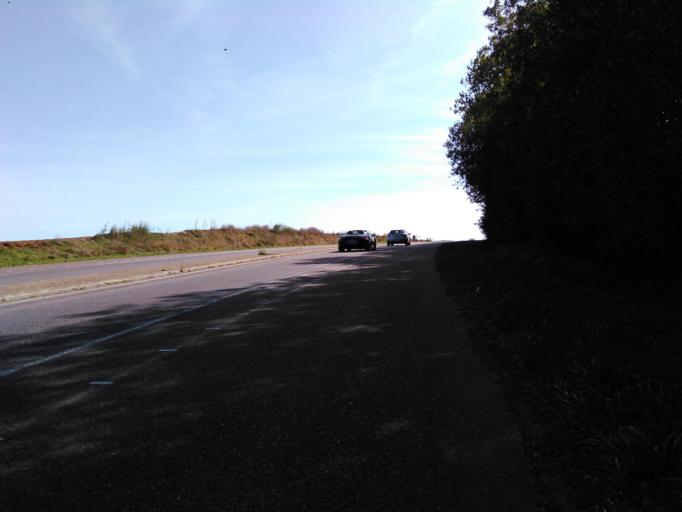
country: FR
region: Lorraine
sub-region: Departement de la Moselle
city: Hettange-Grande
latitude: 49.3912
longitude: 6.1681
